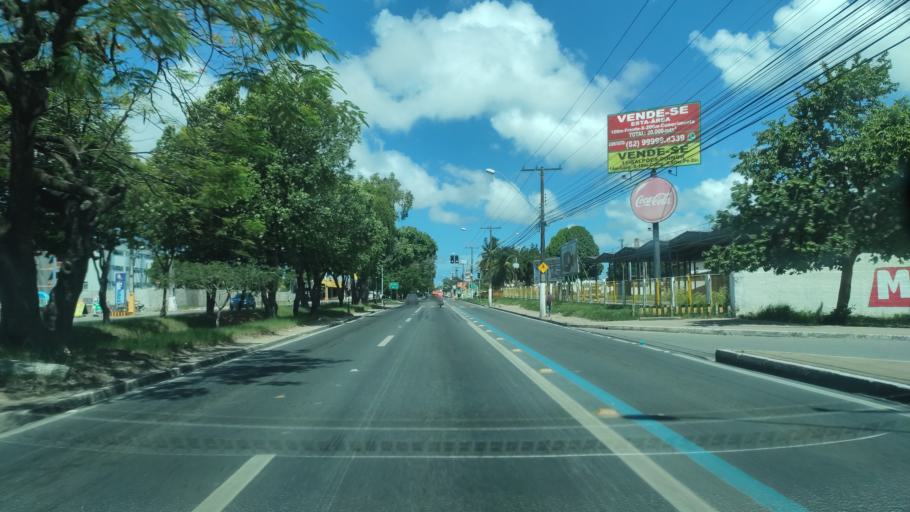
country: BR
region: Alagoas
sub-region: Satuba
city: Satuba
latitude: -9.5838
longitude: -35.7651
